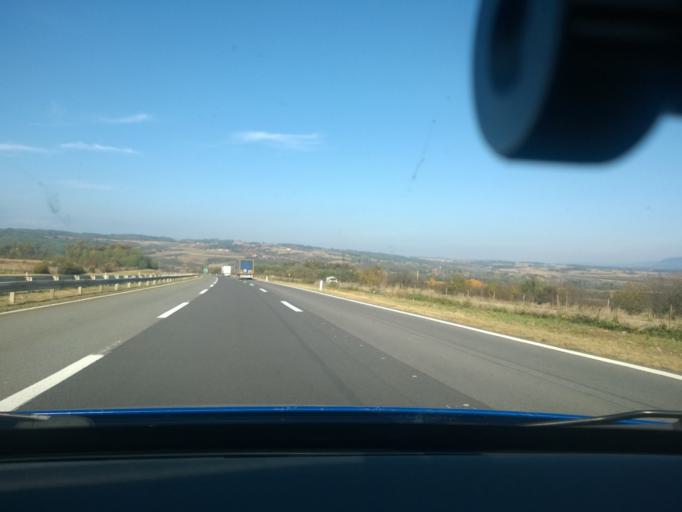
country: RS
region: Central Serbia
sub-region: Nisavski Okrug
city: Razanj
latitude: 43.7347
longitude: 21.5177
